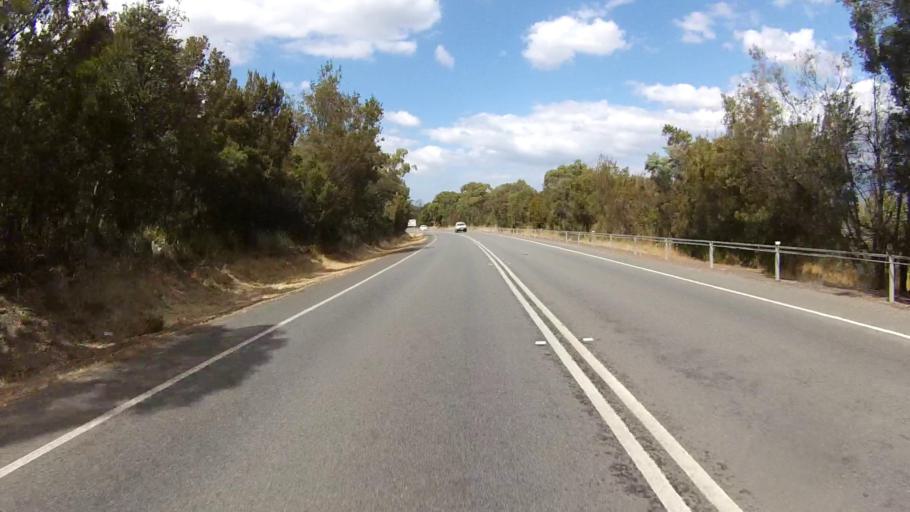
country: AU
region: Tasmania
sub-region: Brighton
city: Old Beach
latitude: -42.7753
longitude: 147.2696
